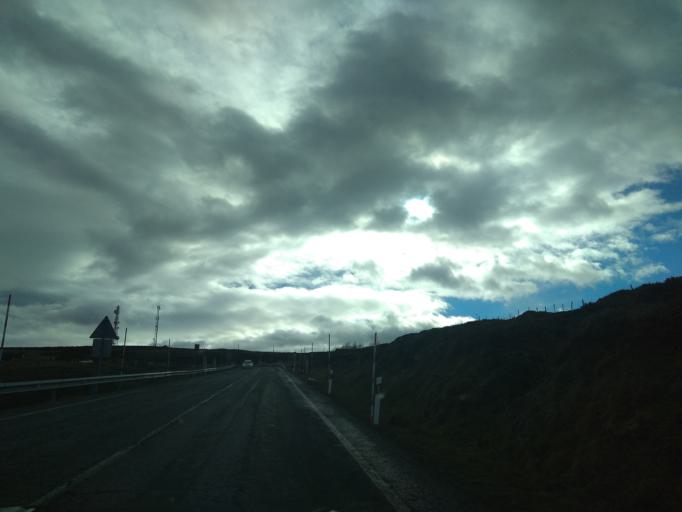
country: ES
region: Castille and Leon
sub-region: Provincia de Burgos
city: Arija
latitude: 43.0530
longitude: -3.8847
